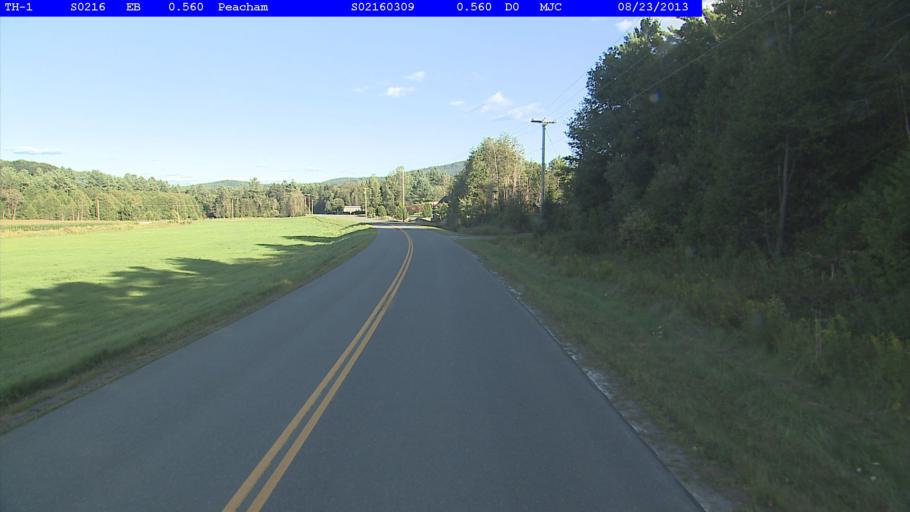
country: US
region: Vermont
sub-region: Caledonia County
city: Saint Johnsbury
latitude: 44.3104
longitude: -72.1572
